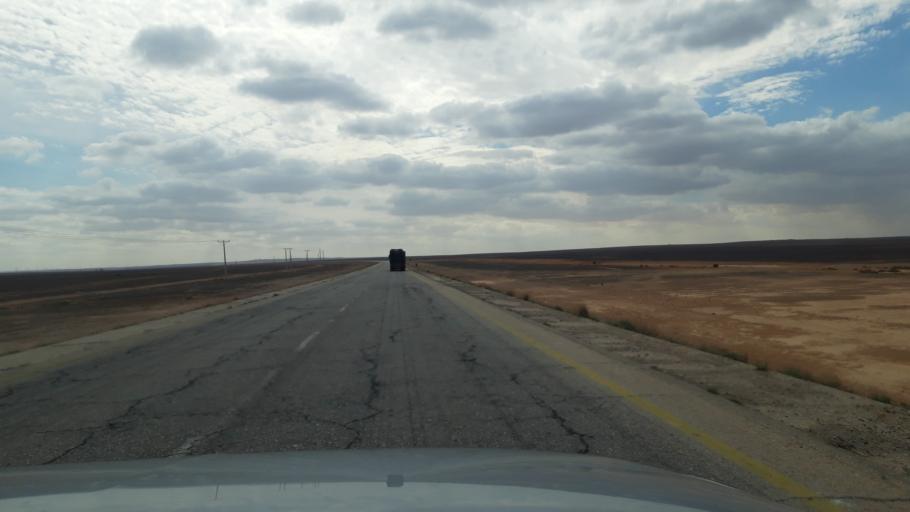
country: JO
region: Amman
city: Al Azraq ash Shamali
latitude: 31.8233
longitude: 36.6092
